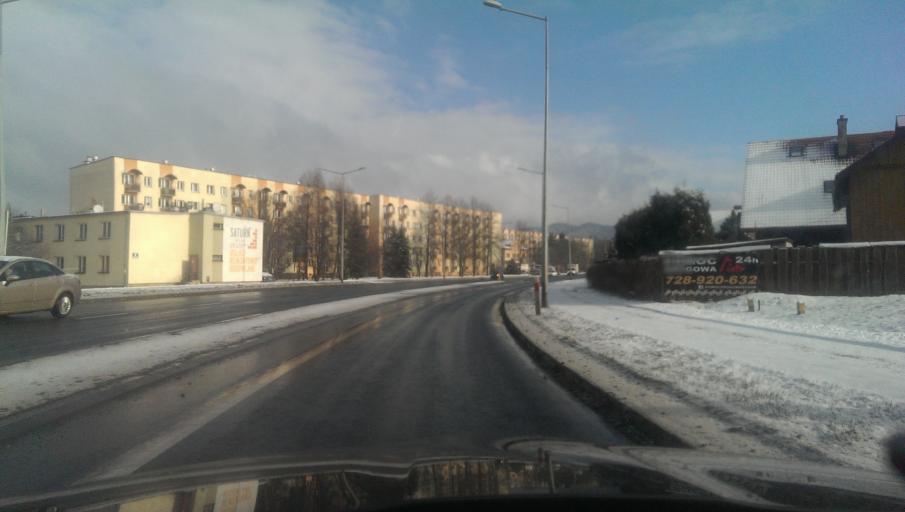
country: PL
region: Subcarpathian Voivodeship
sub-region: Powiat sanocki
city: Sanok
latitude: 49.5655
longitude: 22.1946
